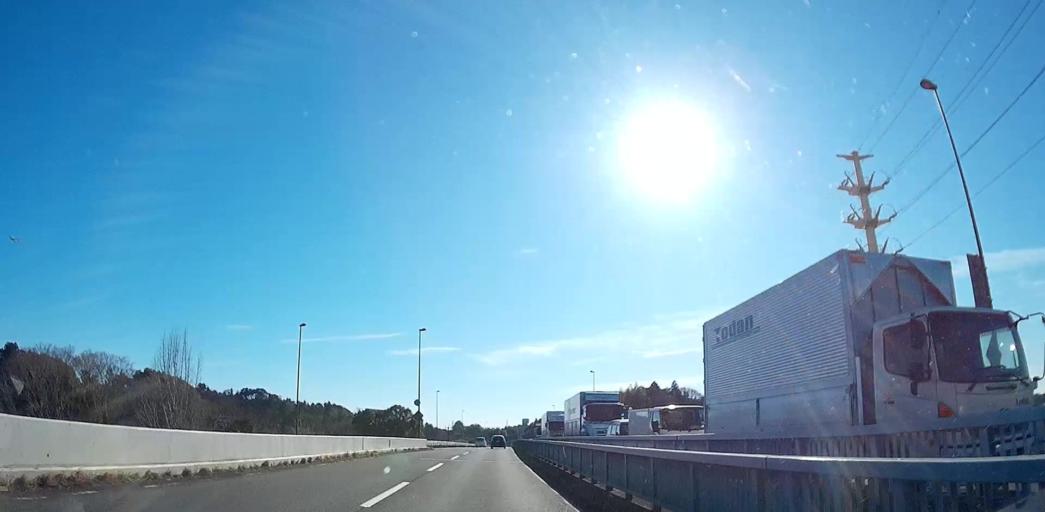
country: JP
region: Chiba
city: Narita
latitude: 35.7889
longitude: 140.3304
